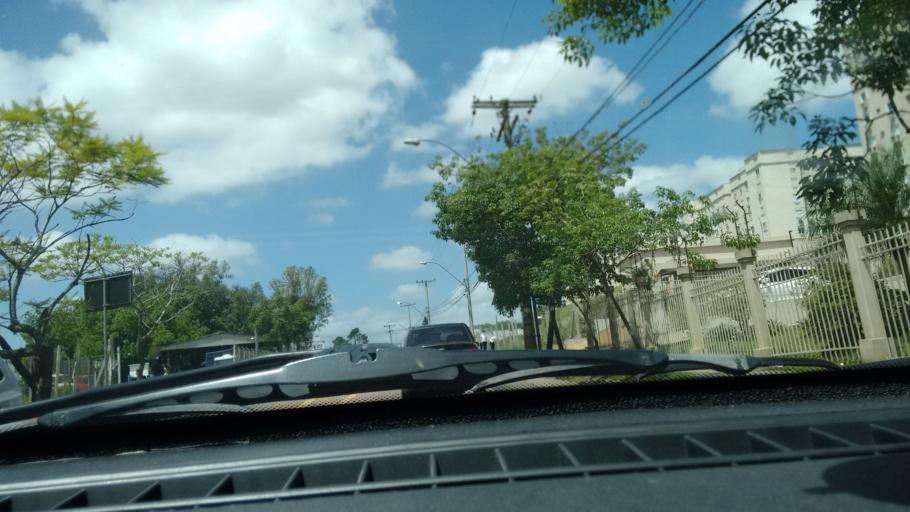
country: BR
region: Rio Grande do Sul
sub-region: Cachoeirinha
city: Cachoeirinha
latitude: -30.0043
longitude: -51.1276
